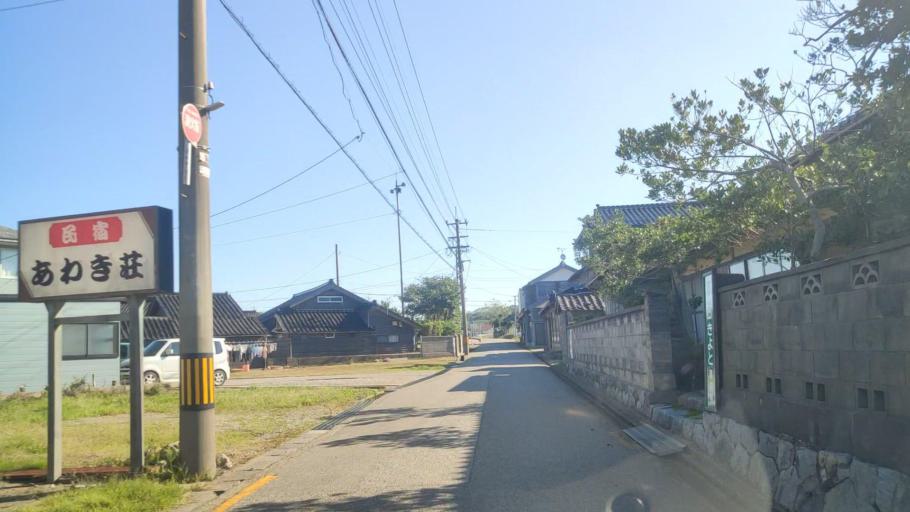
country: JP
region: Ishikawa
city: Hakui
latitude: 36.9523
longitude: 136.7659
